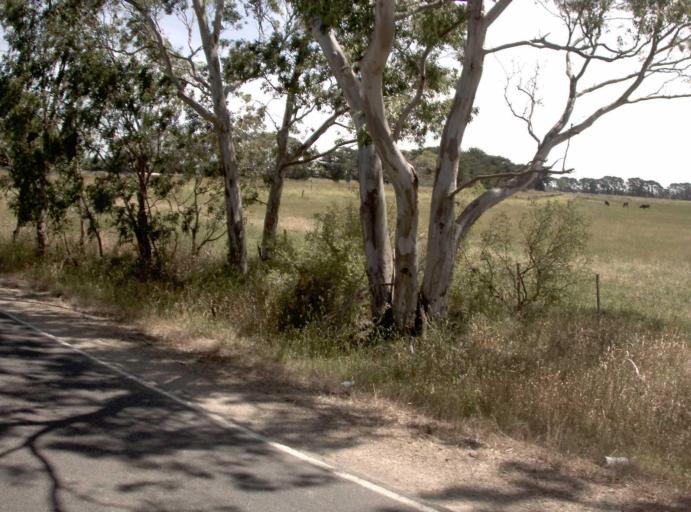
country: AU
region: Victoria
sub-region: Wellington
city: Heyfield
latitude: -38.0425
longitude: 146.8767
